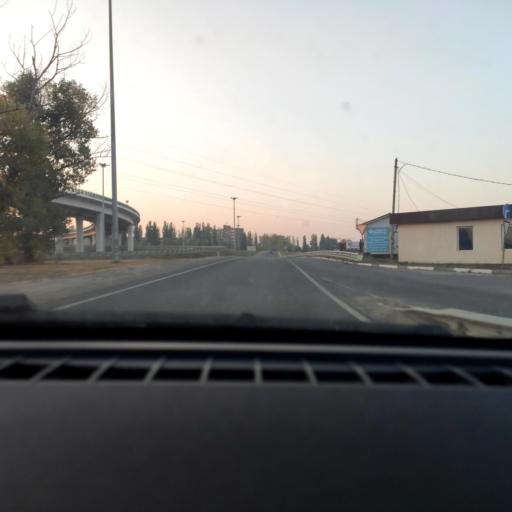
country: RU
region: Voronezj
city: Novaya Usman'
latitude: 51.6510
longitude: 39.2982
